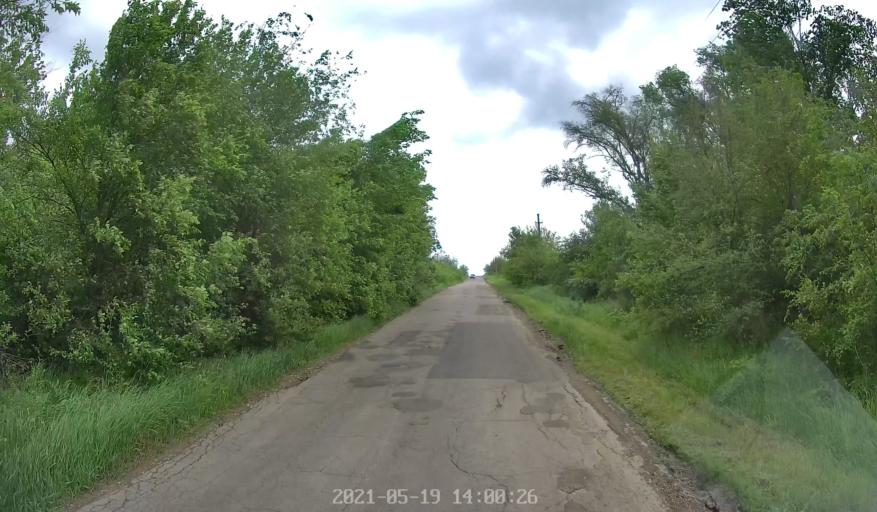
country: MD
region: Chisinau
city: Chisinau
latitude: 47.0349
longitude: 28.9320
